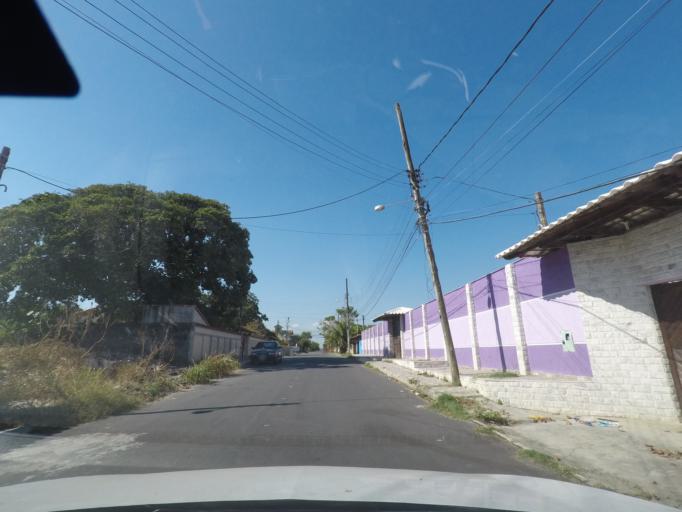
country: BR
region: Rio de Janeiro
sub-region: Marica
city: Marica
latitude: -22.9704
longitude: -42.9235
